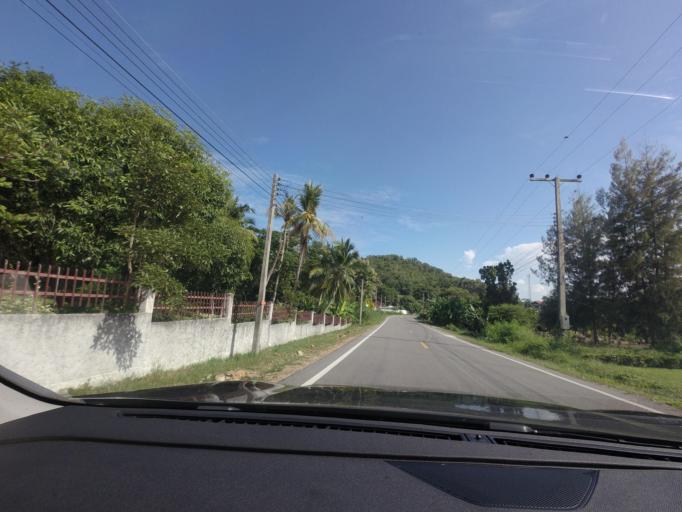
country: TH
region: Prachuap Khiri Khan
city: Pran Buri
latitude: 12.4592
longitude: 99.9448
